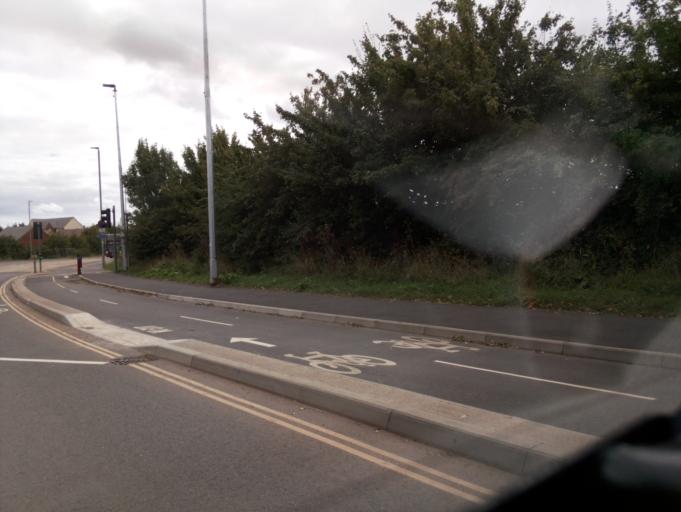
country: GB
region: England
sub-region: Devon
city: Heavitree
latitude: 50.7362
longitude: -3.4764
